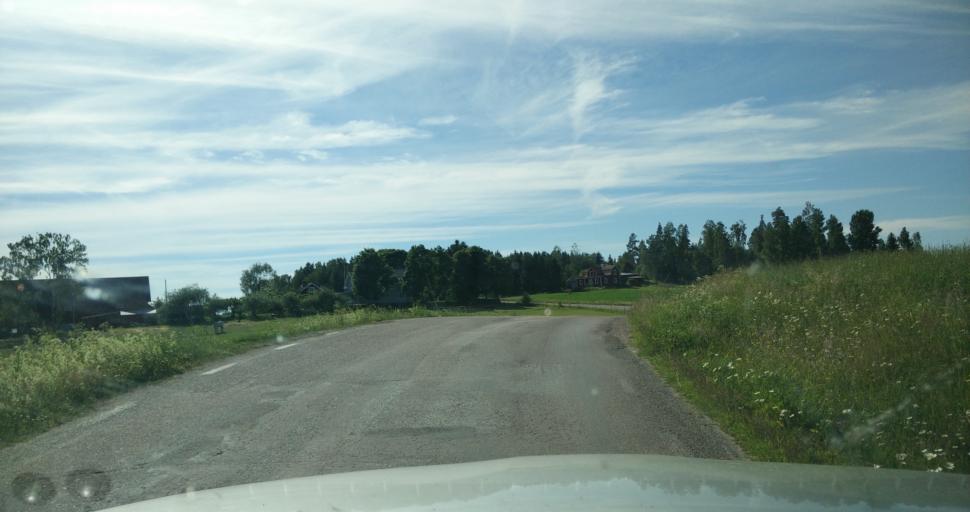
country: SE
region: Dalarna
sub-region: Hedemora Kommun
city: Langshyttan
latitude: 60.3938
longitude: 15.9458
